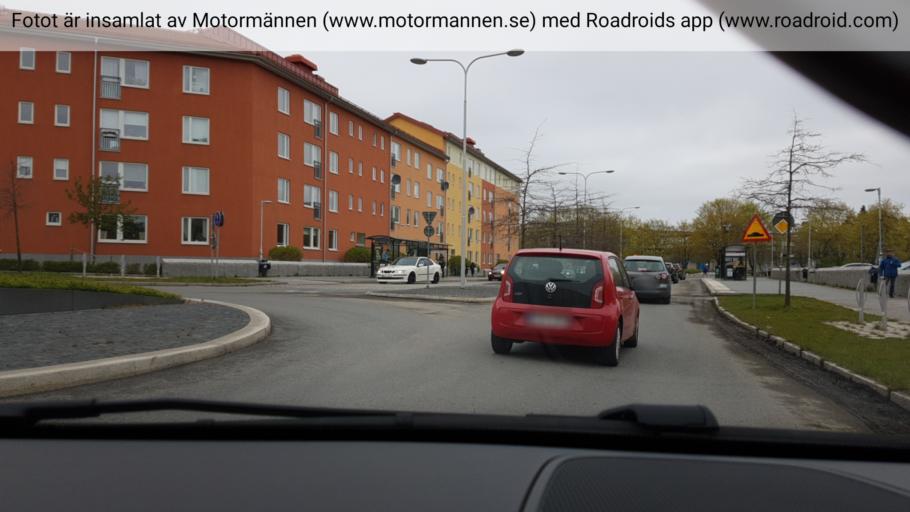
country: SE
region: Stockholm
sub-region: Huddinge Kommun
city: Huddinge
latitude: 59.2406
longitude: 17.9944
